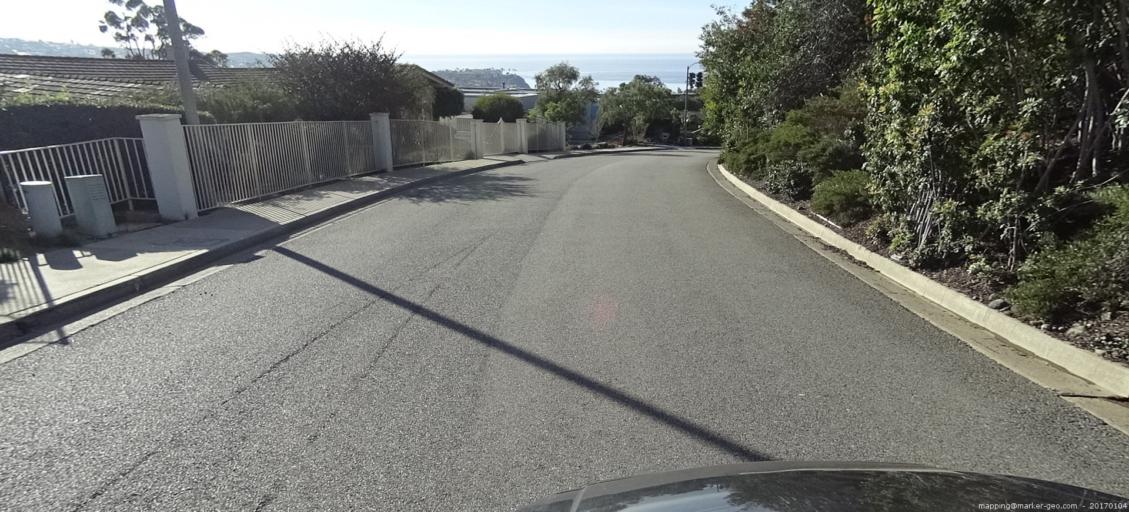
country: US
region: California
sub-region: Orange County
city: Dana Point
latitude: 33.4906
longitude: -117.7218
